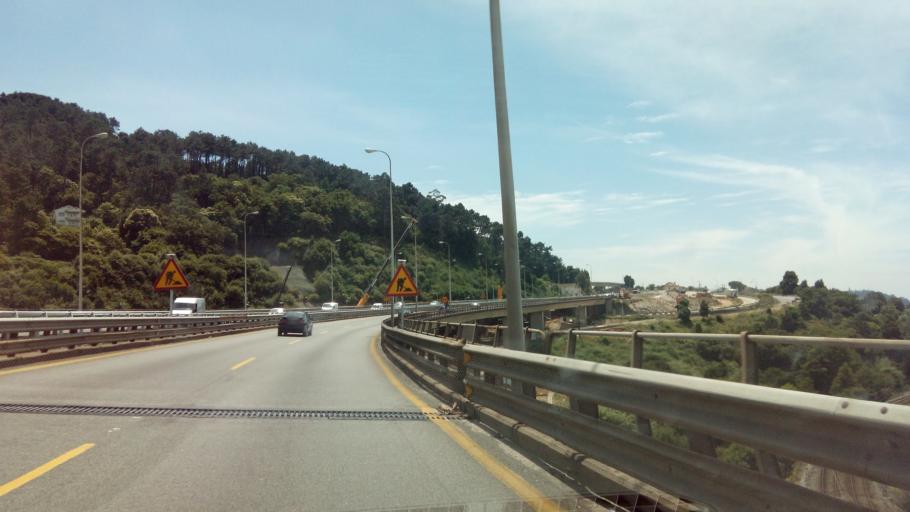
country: ES
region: Galicia
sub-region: Provincia de Pontevedra
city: Redondela
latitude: 42.2816
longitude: -8.6614
